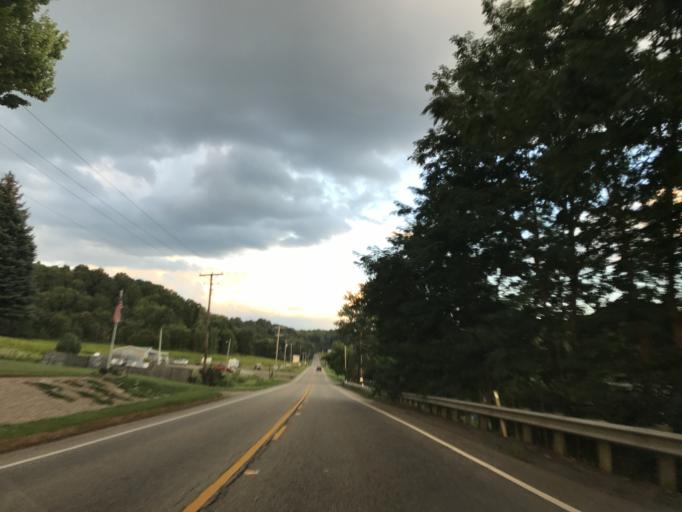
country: US
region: Ohio
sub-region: Stark County
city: Minerva
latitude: 40.7380
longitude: -81.1442
